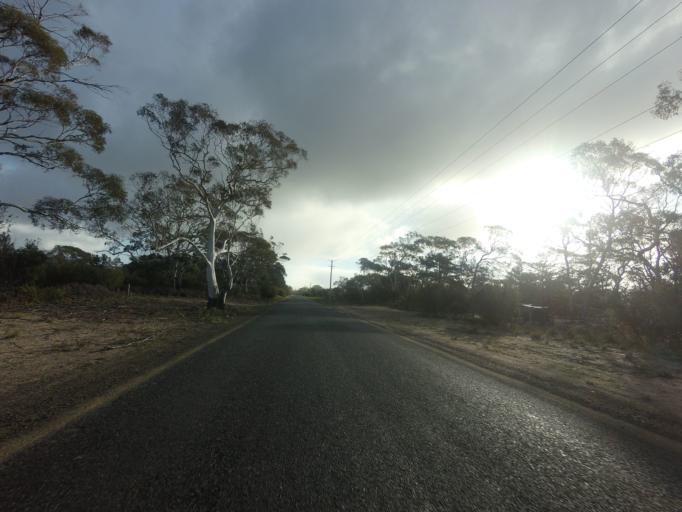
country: AU
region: Tasmania
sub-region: Break O'Day
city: St Helens
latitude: -42.0904
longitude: 148.1166
